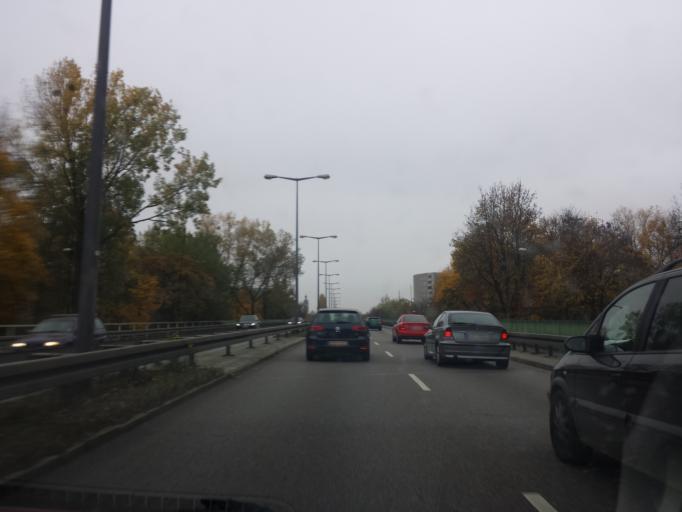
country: DE
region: Bavaria
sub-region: Upper Bavaria
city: Munich
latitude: 48.1683
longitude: 11.5381
